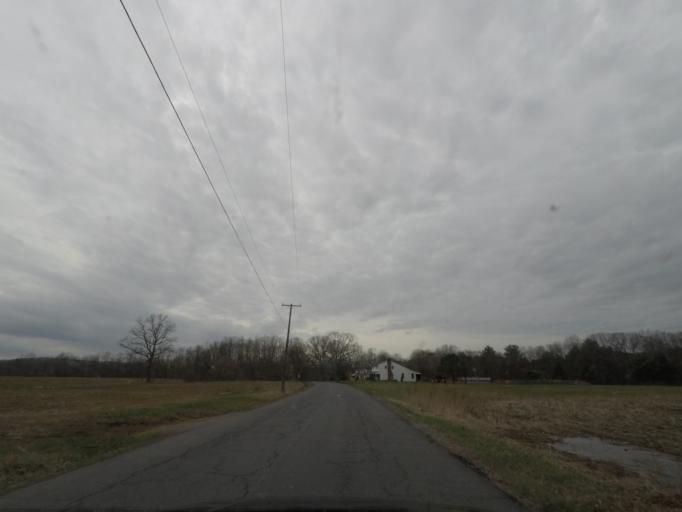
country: US
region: New York
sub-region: Rensselaer County
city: Castleton-on-Hudson
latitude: 42.5621
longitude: -73.7978
